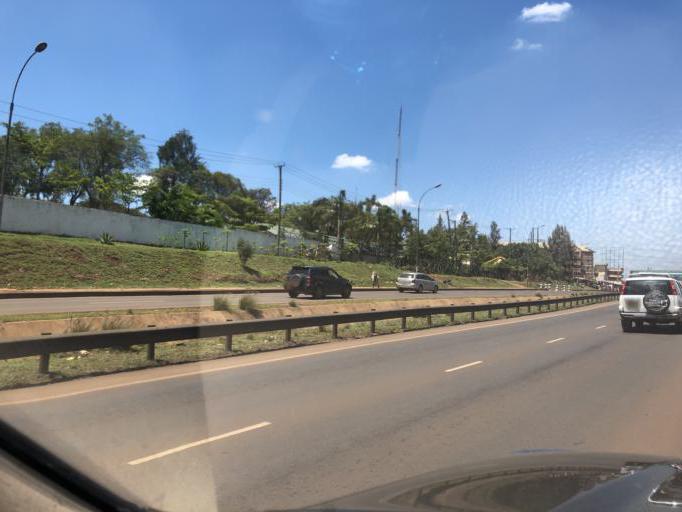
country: KE
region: Kiambu
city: Kiambu
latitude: -1.2152
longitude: 36.8965
